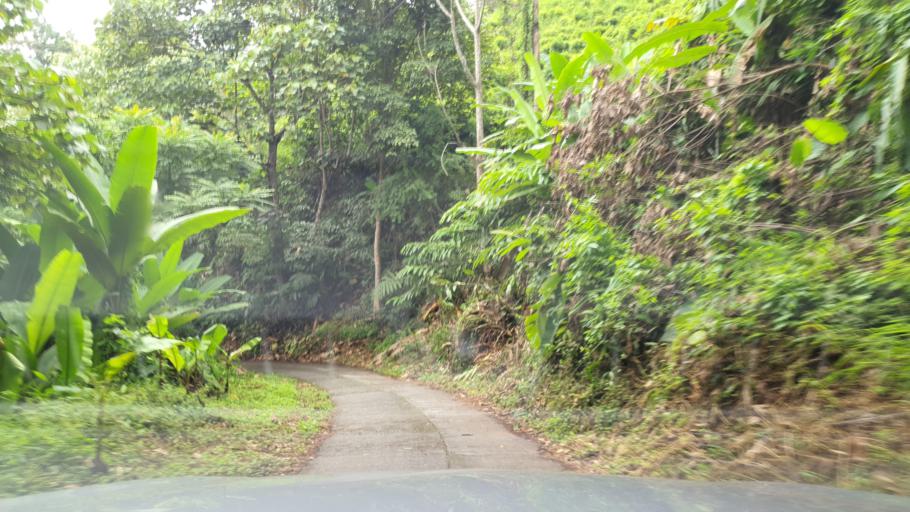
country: TH
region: Chiang Mai
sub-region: Amphoe Chiang Dao
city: Chiang Dao
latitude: 19.2675
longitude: 98.9305
